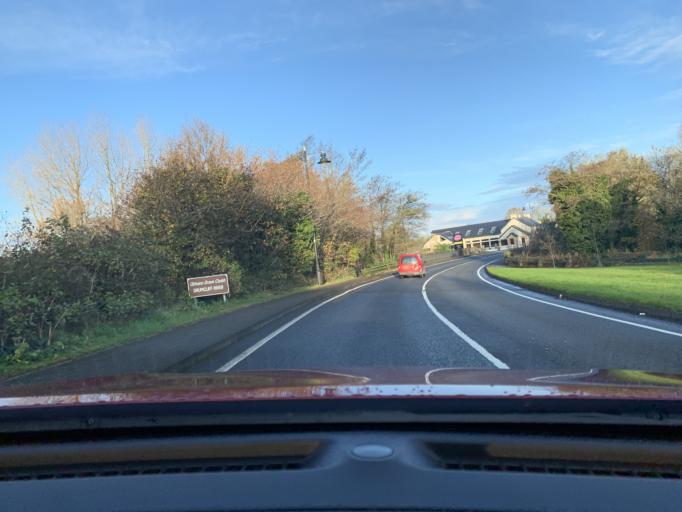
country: IE
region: Connaught
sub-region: Sligo
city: Sligo
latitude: 54.3276
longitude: -8.5002
